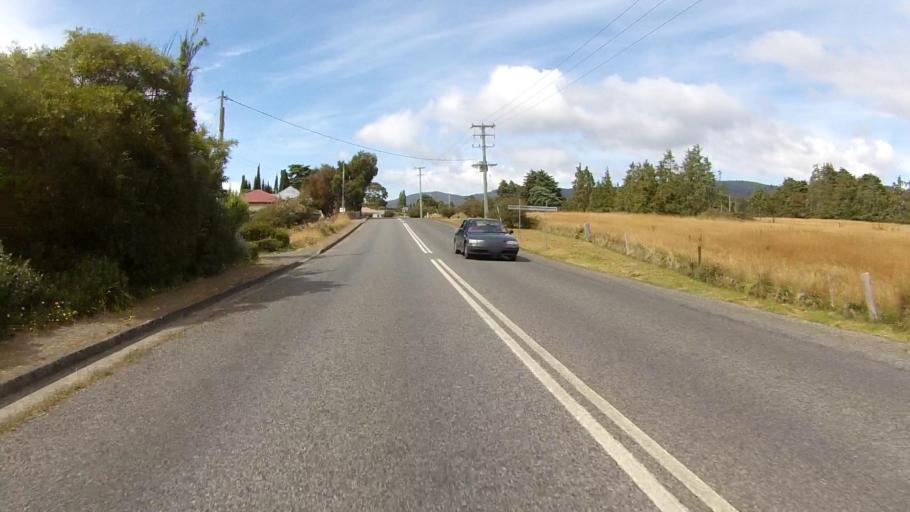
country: AU
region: Tasmania
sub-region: Kingborough
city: Kettering
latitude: -43.1545
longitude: 147.2378
